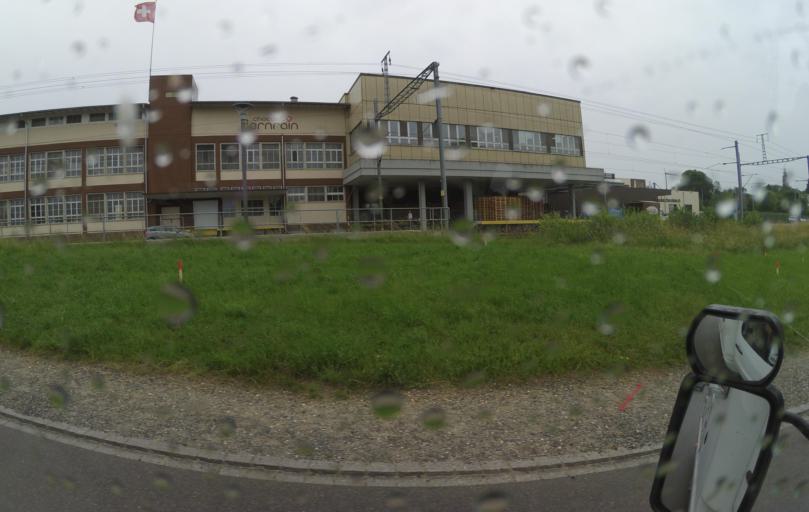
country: DE
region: Baden-Wuerttemberg
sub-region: Freiburg Region
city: Konstanz
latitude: 47.6428
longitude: 9.1615
